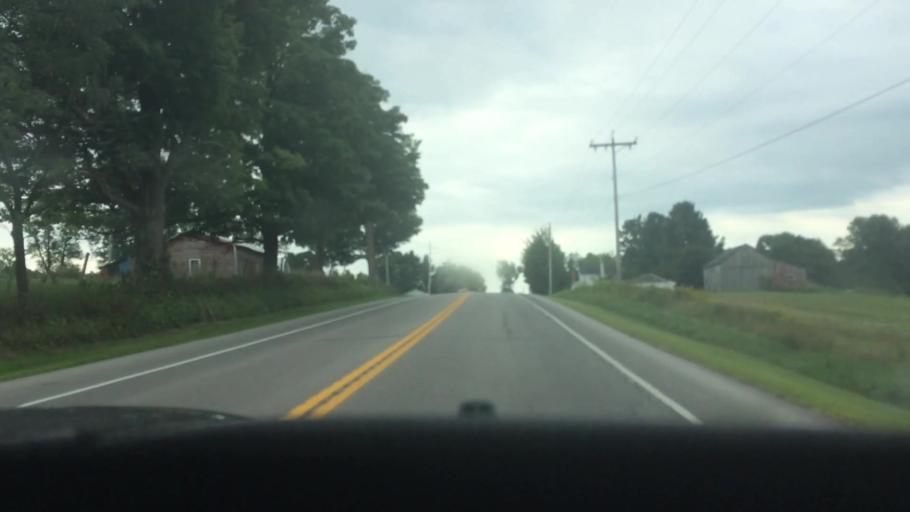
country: US
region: New York
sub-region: St. Lawrence County
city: Ogdensburg
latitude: 44.6104
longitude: -75.3977
